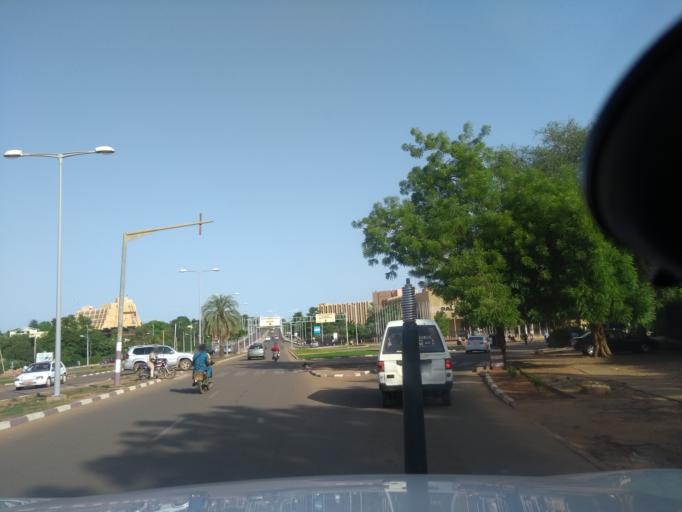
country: NE
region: Niamey
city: Niamey
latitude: 13.5113
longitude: 2.1046
